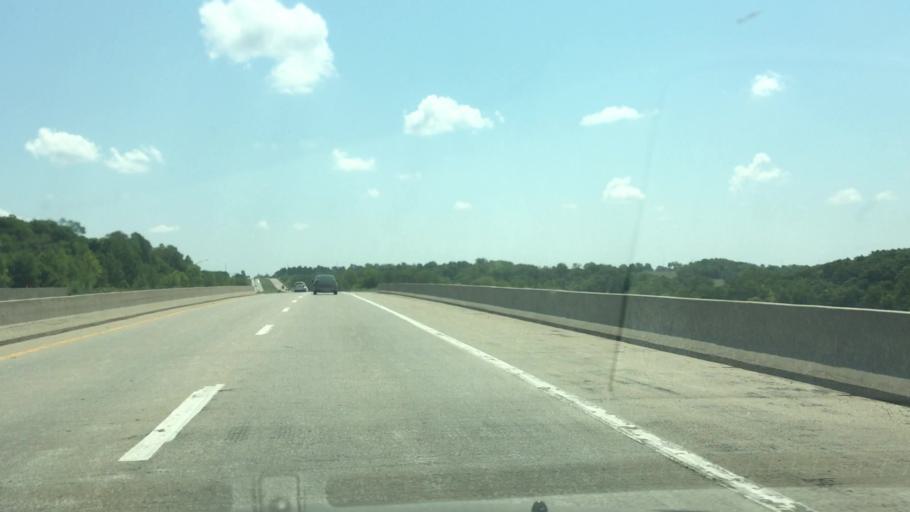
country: US
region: Missouri
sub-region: Jackson County
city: Grandview
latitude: 38.8621
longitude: -94.5859
